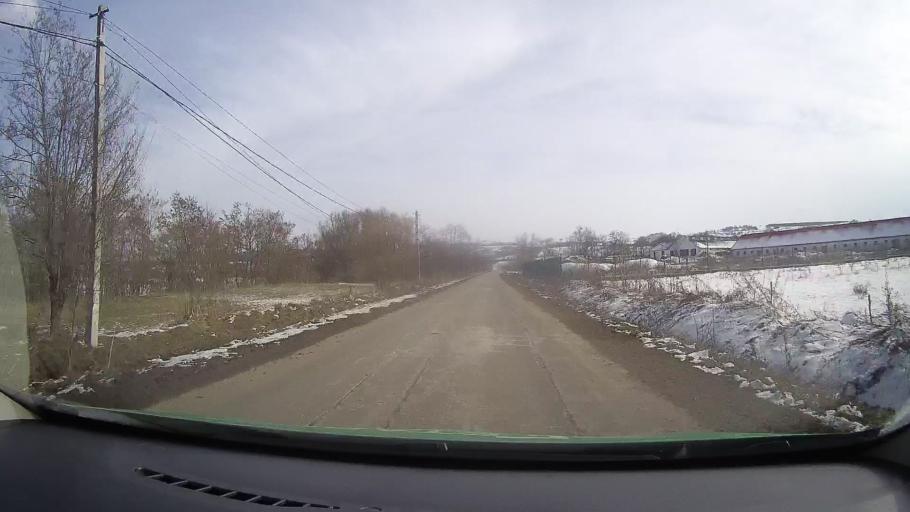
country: RO
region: Mures
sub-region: Comuna Apold
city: Apold
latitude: 46.1205
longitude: 24.8227
